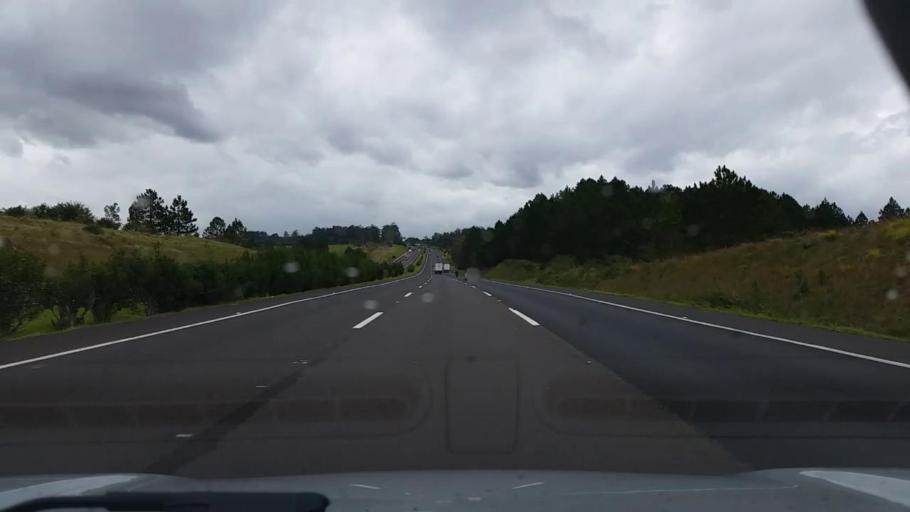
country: BR
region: Rio Grande do Sul
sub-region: Gravatai
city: Gravatai
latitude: -29.9256
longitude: -50.8617
